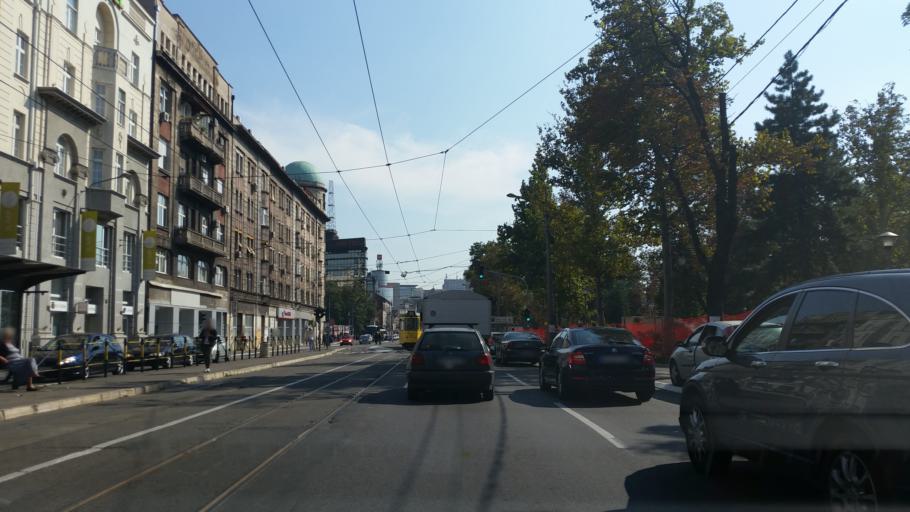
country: RS
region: Central Serbia
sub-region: Belgrade
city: Stari Grad
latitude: 44.8123
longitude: 20.4533
